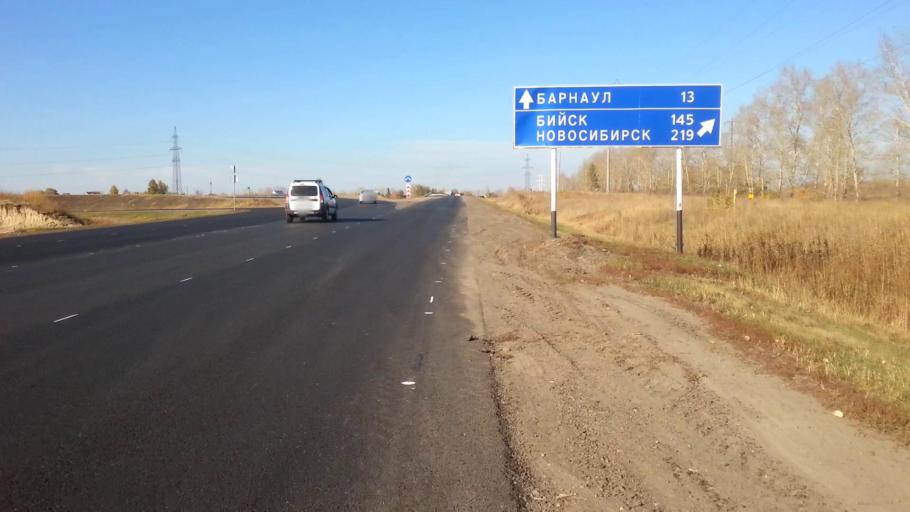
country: RU
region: Altai Krai
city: Sannikovo
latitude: 53.3381
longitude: 83.9387
